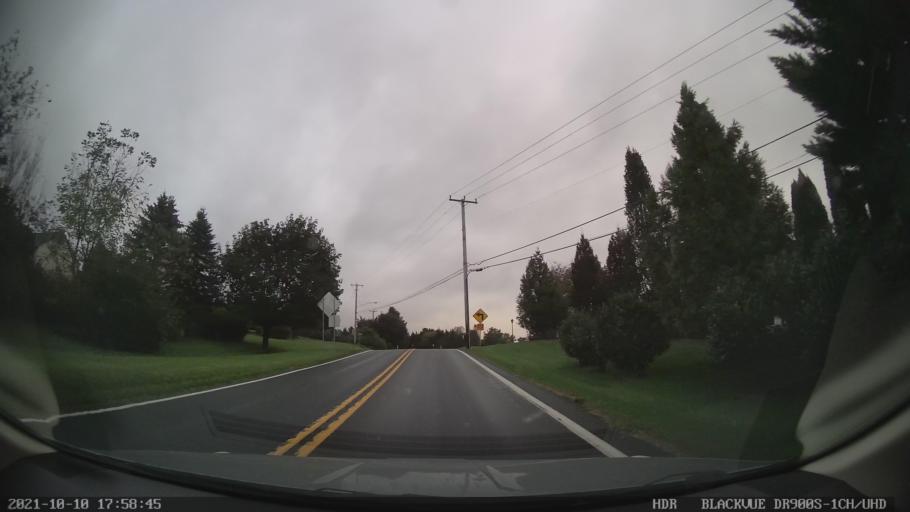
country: US
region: Pennsylvania
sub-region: Lehigh County
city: Schnecksville
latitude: 40.6362
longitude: -75.5685
